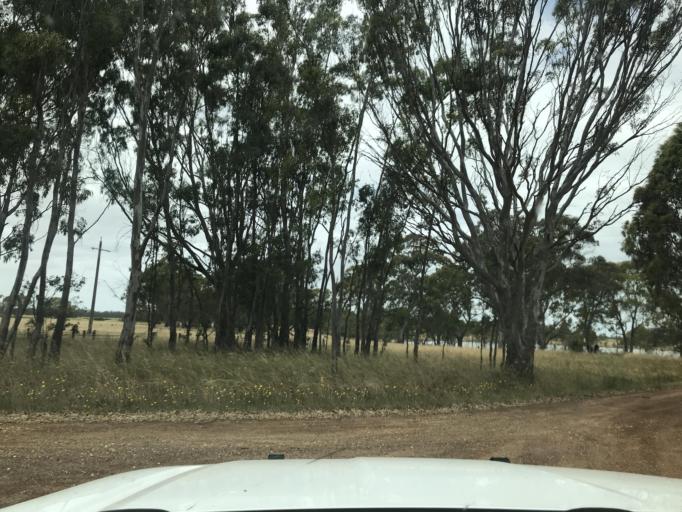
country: AU
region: South Australia
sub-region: Naracoorte and Lucindale
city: Naracoorte
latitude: -37.0000
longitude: 141.3505
